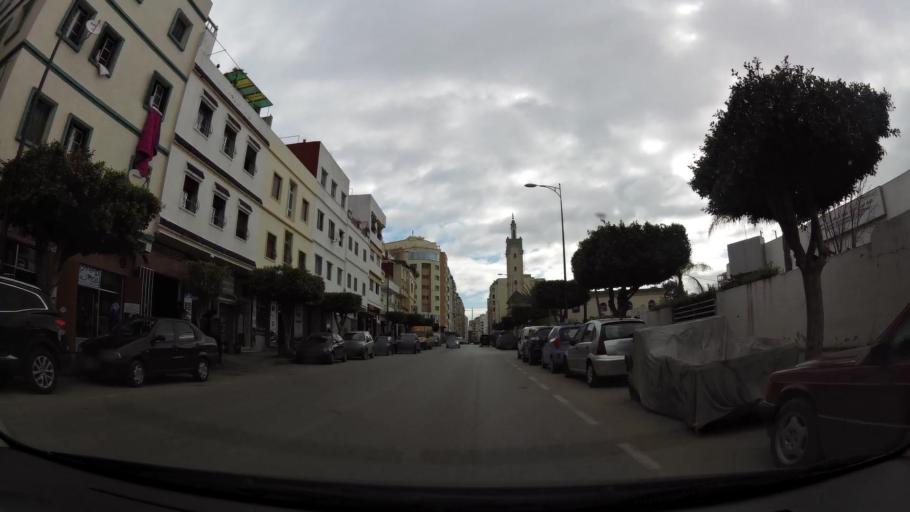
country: MA
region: Tanger-Tetouan
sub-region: Tanger-Assilah
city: Tangier
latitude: 35.7710
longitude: -5.8182
